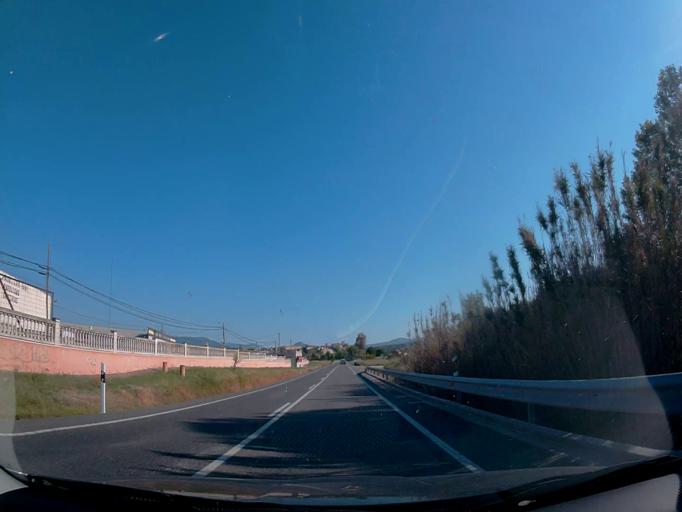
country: ES
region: Castille-La Mancha
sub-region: Province of Toledo
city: Escalona
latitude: 40.1516
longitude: -4.4026
